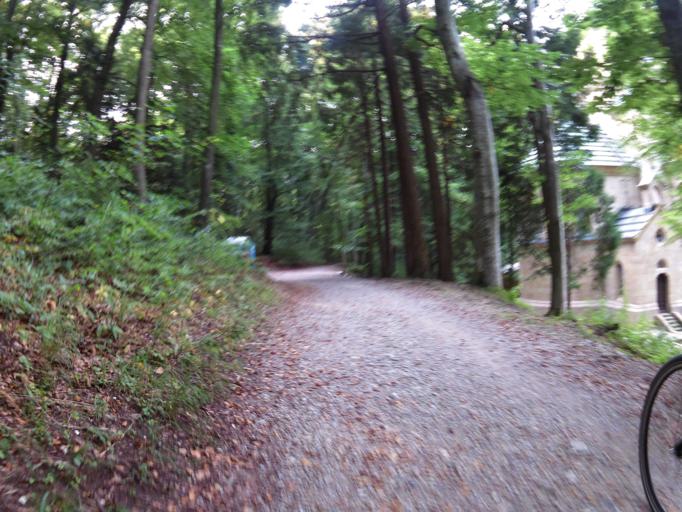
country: DE
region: Bavaria
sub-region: Upper Bavaria
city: Berg
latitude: 47.9641
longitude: 11.3486
